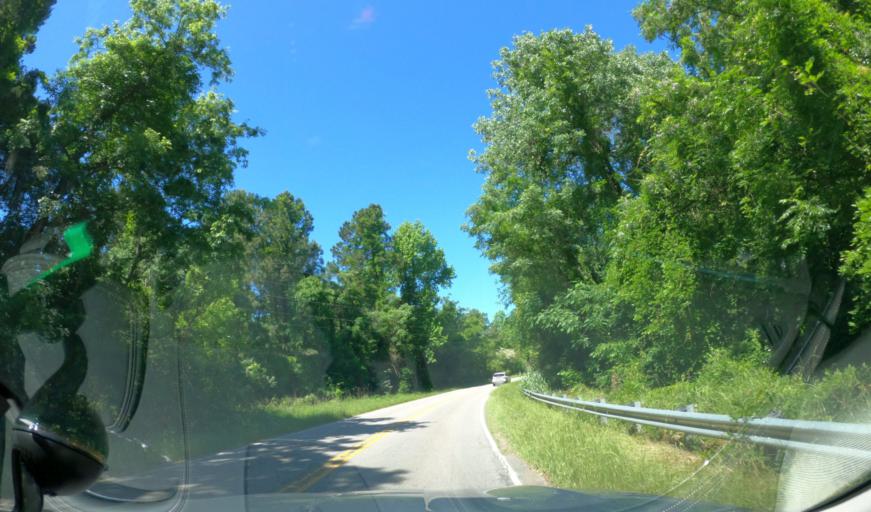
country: US
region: South Carolina
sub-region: Aiken County
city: Clearwater
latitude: 33.4660
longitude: -81.8686
